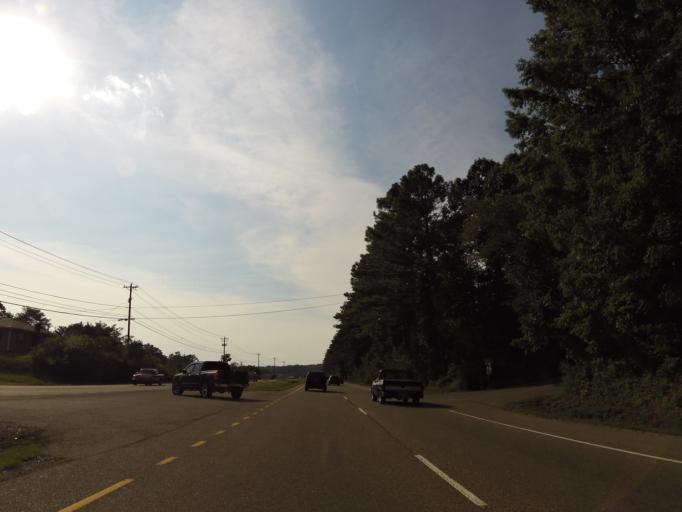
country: US
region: Tennessee
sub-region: Loudon County
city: Lenoir City
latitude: 35.8327
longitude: -84.2859
